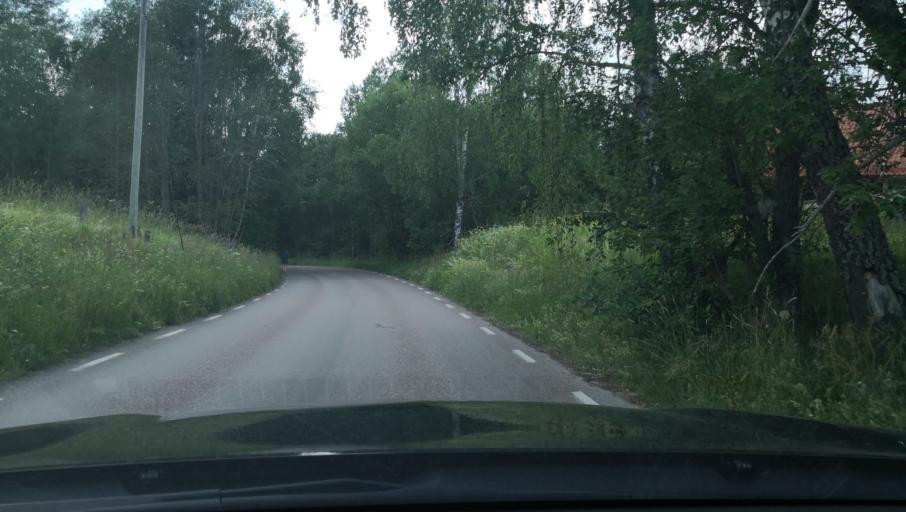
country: SE
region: Dalarna
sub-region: Smedjebackens Kommun
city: Smedjebacken
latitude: 60.0489
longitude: 15.5323
